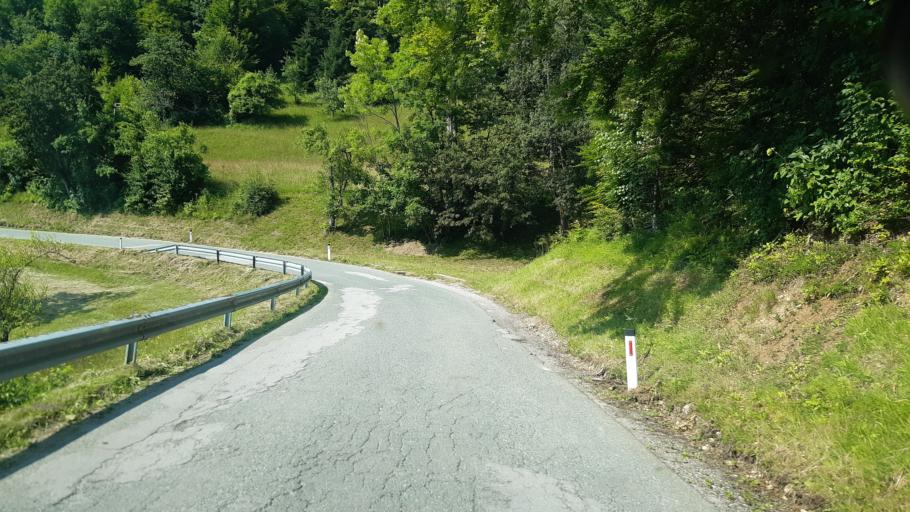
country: SI
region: Trzic
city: Bistrica pri Trzicu
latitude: 46.3613
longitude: 14.2433
